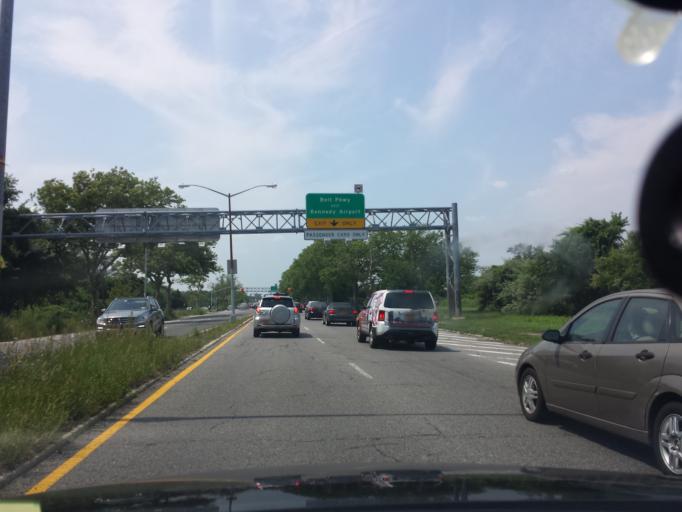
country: US
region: New York
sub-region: Kings County
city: Brooklyn
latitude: 40.5924
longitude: -73.9033
